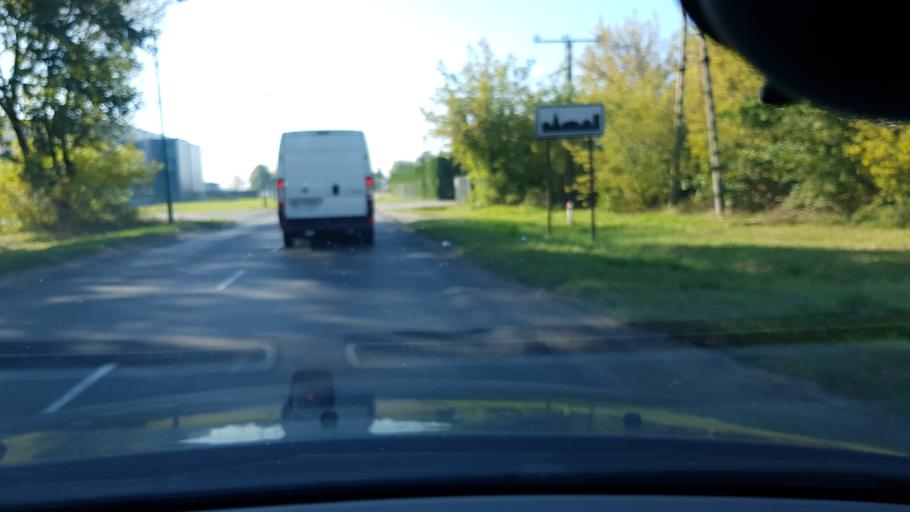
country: PL
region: Lodz Voivodeship
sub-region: Powiat tomaszowski
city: Tomaszow Mazowiecki
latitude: 51.5606
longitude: 20.0208
